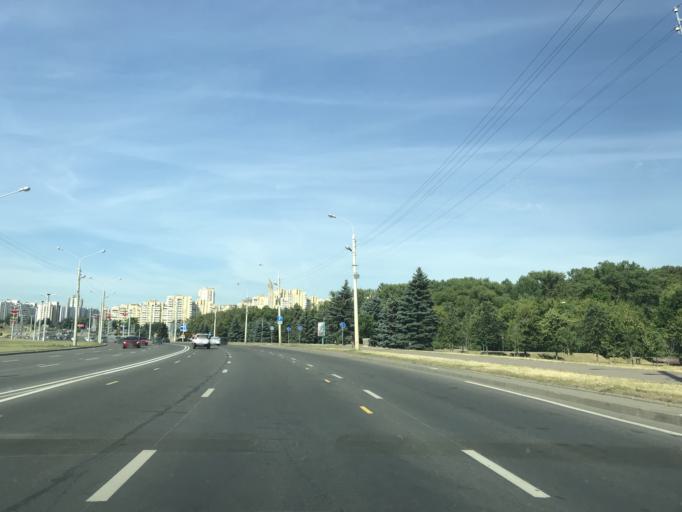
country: BY
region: Minsk
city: Minsk
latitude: 53.9175
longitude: 27.5462
